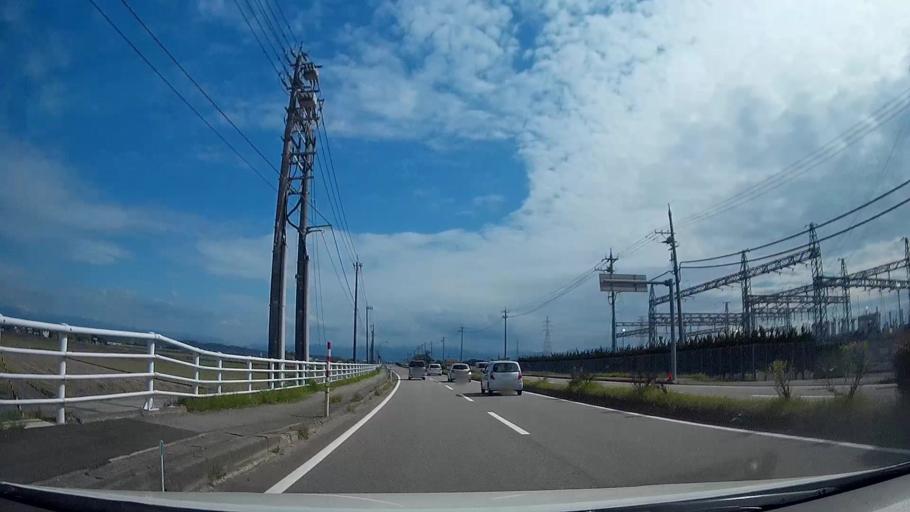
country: JP
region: Toyama
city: Kuragaki-kosugi
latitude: 36.7467
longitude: 137.1294
